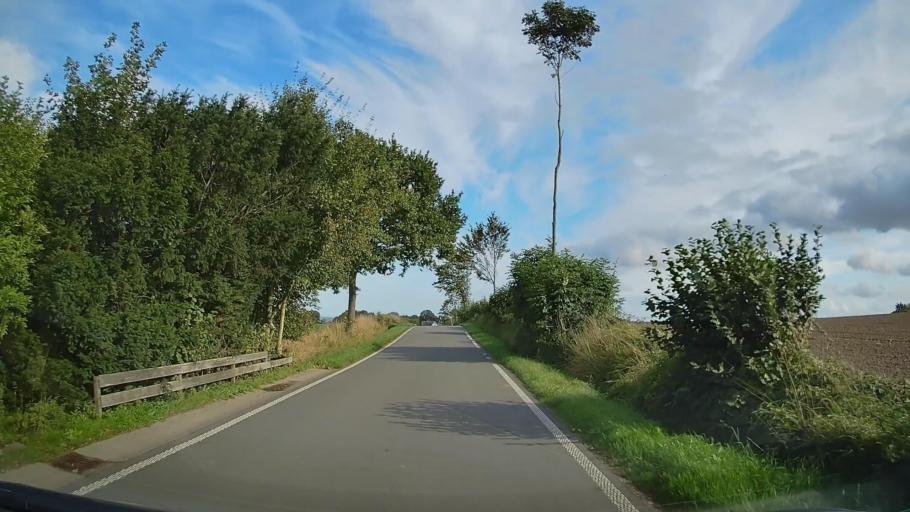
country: DE
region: Schleswig-Holstein
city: Steinbergkirche
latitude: 54.8010
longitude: 9.7476
